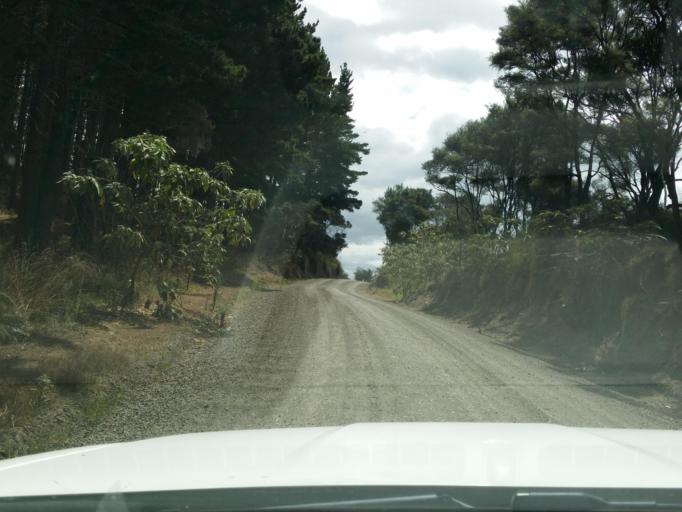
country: NZ
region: Auckland
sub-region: Auckland
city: Wellsford
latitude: -36.3052
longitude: 174.1171
